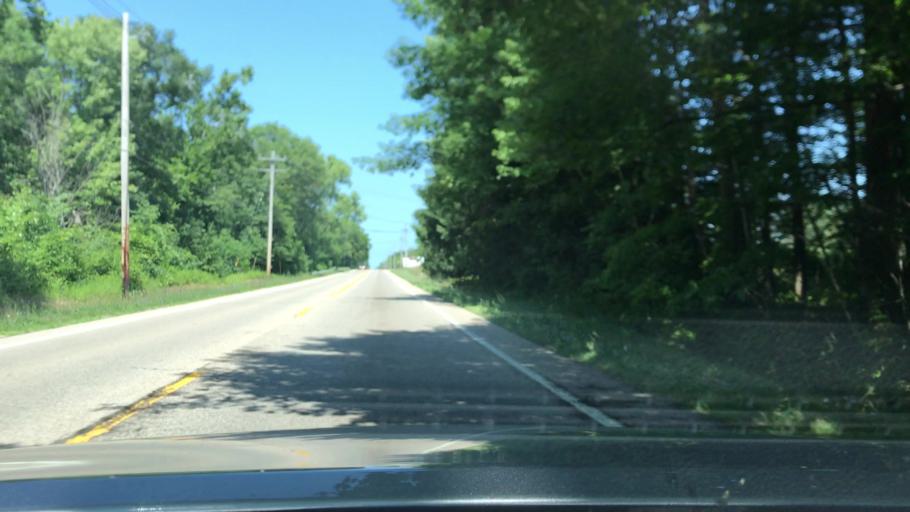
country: US
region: Michigan
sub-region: Ottawa County
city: Allendale
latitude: 42.9339
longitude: -86.0820
